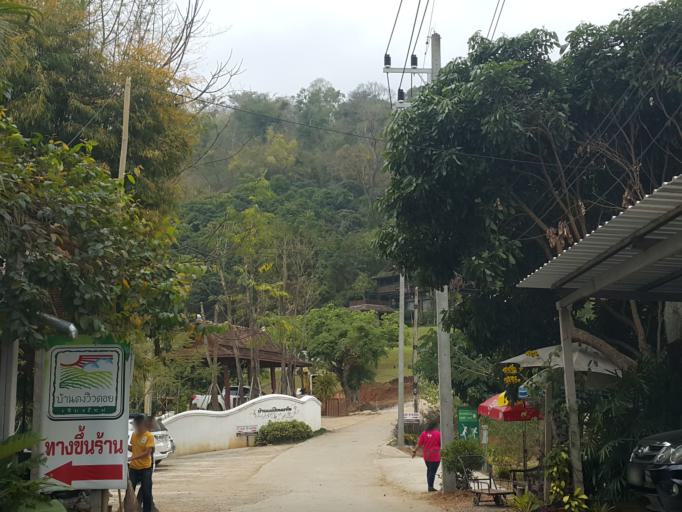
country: TH
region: Chiang Mai
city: Hang Dong
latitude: 18.7837
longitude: 98.8422
